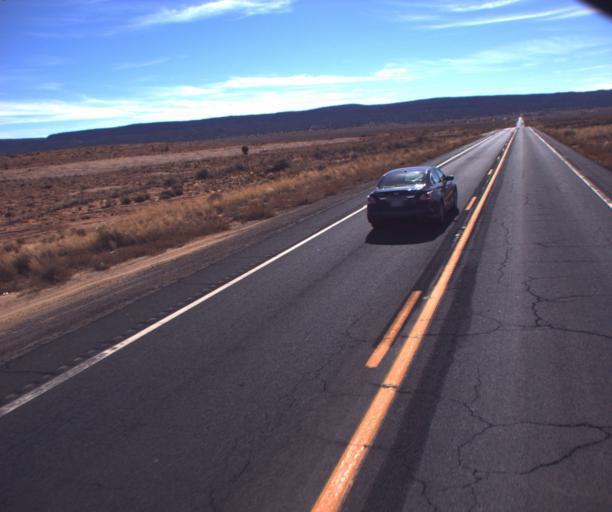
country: US
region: Arizona
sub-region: Coconino County
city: Kaibito
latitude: 36.4807
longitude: -110.7031
